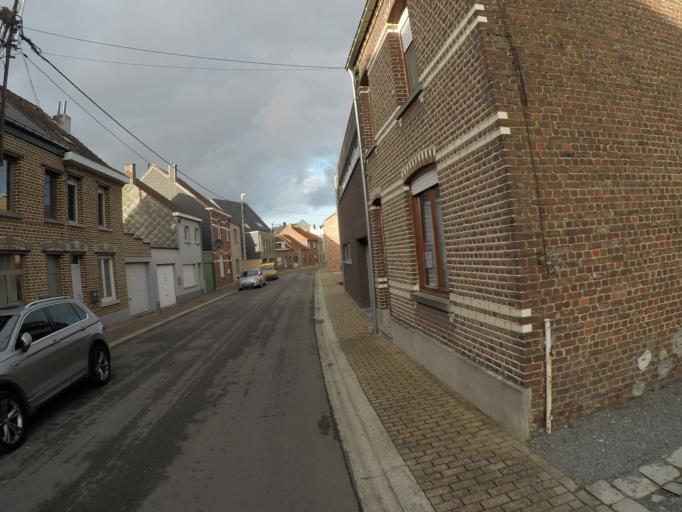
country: BE
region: Flanders
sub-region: Provincie Vlaams-Brabant
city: Opwijk
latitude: 50.9670
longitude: 4.1919
